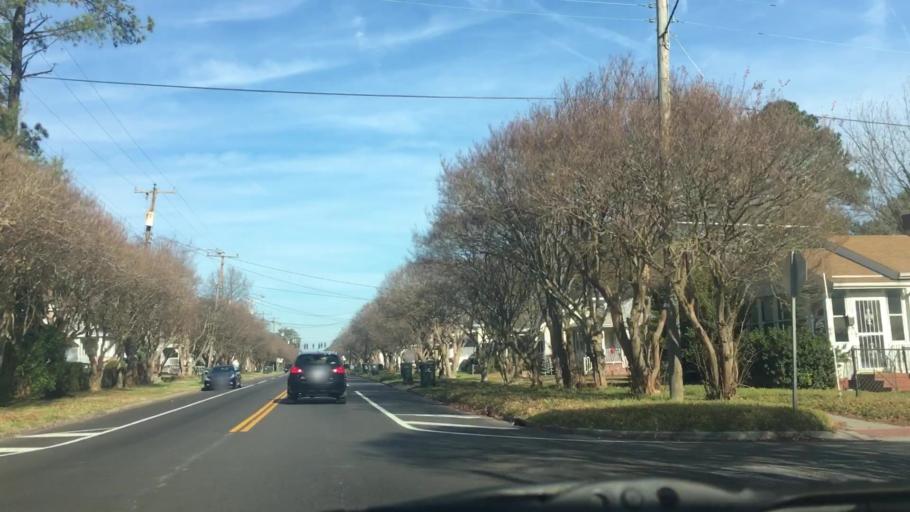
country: US
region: Virginia
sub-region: City of Norfolk
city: Norfolk
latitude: 36.8659
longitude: -76.2511
